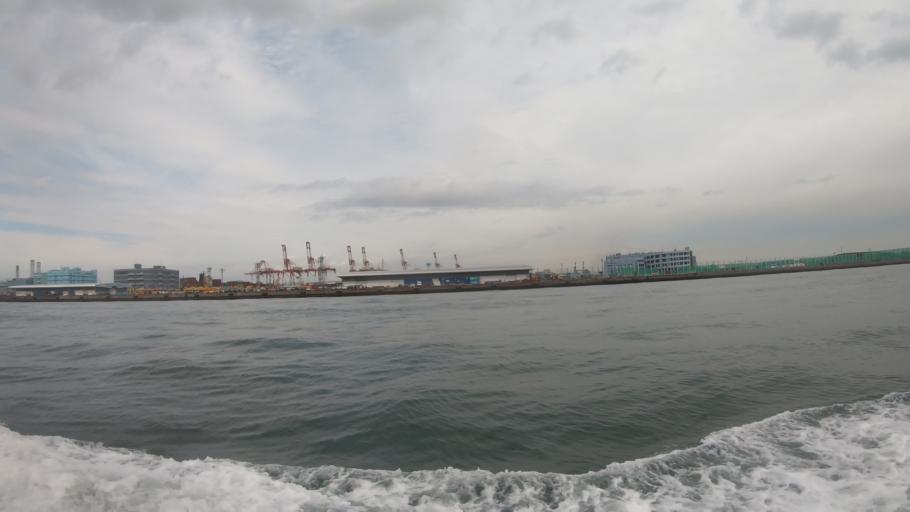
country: JP
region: Kanagawa
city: Yokohama
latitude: 35.4506
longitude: 139.6893
